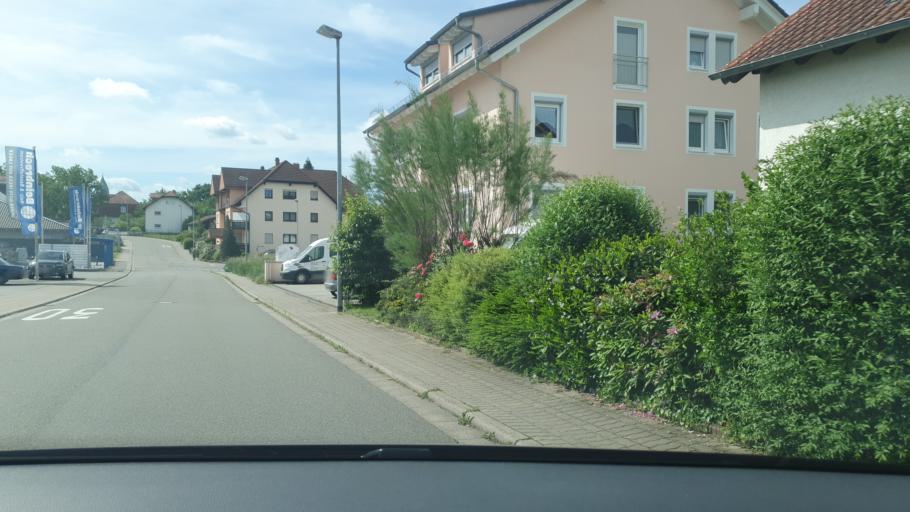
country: DE
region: Rheinland-Pfalz
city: Ramstein-Miesenbach
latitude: 49.4510
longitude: 7.5524
